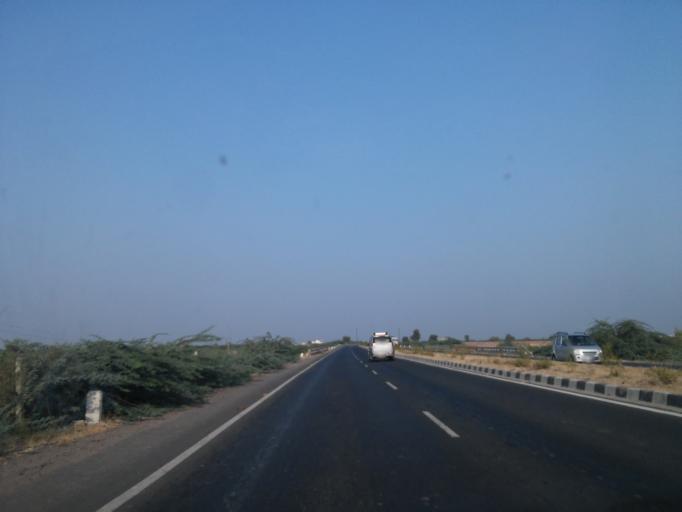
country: IN
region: Gujarat
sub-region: Surendranagar
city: Lakhtar
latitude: 23.0576
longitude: 71.7229
